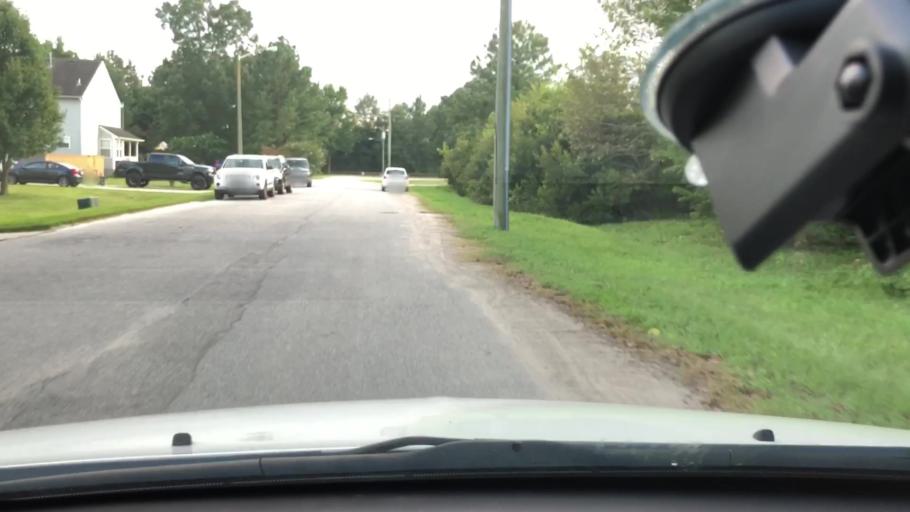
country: US
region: Virginia
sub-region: City of Chesapeake
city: Chesapeake
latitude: 36.7200
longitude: -76.2706
